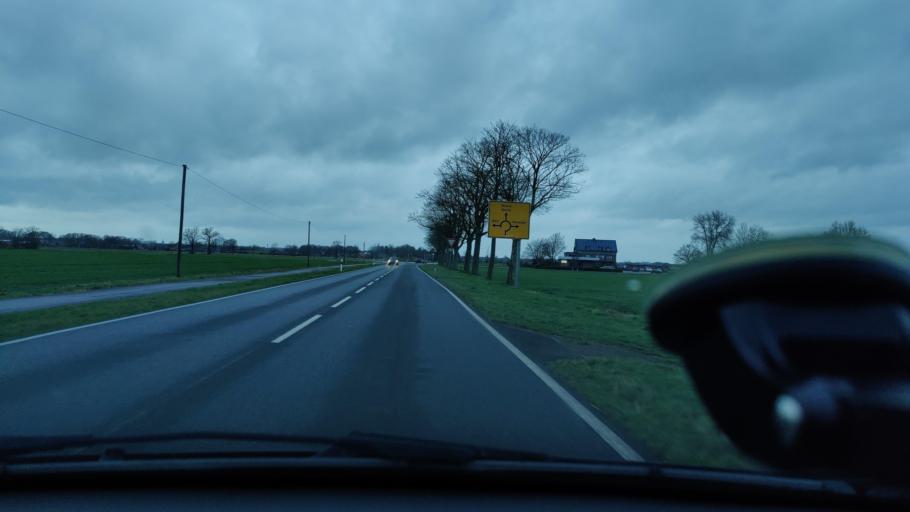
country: DE
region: North Rhine-Westphalia
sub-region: Regierungsbezirk Dusseldorf
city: Weeze
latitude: 51.5715
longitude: 6.1870
